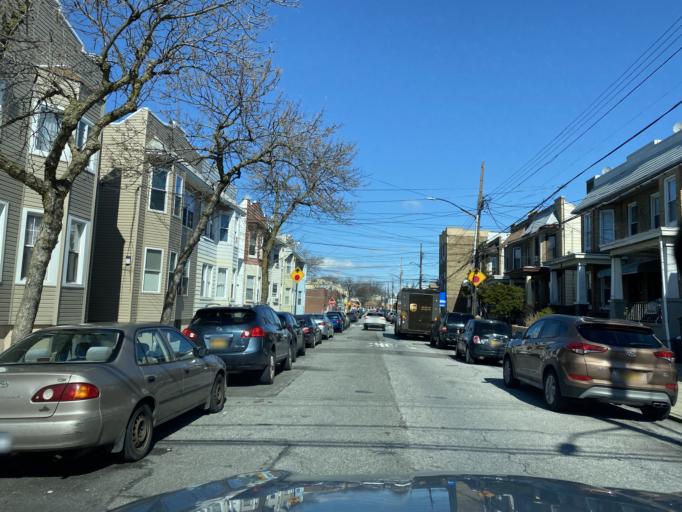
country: US
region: New York
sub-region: Kings County
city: East New York
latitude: 40.7105
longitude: -73.8734
